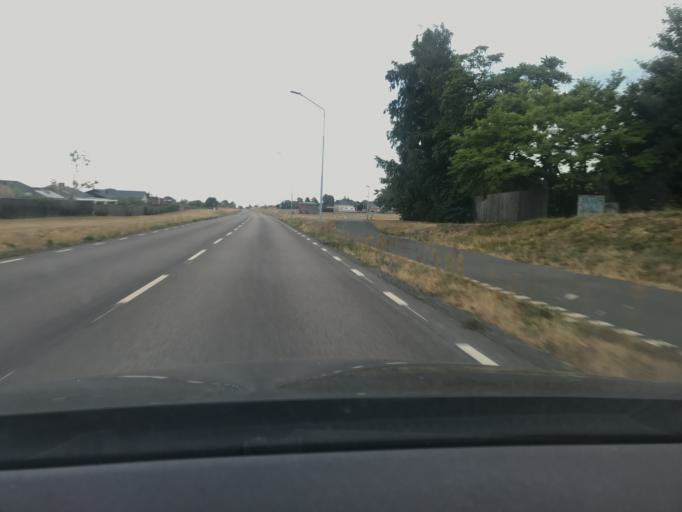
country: SE
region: Skane
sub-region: Simrishamns Kommun
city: Simrishamn
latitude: 55.5474
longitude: 14.3505
